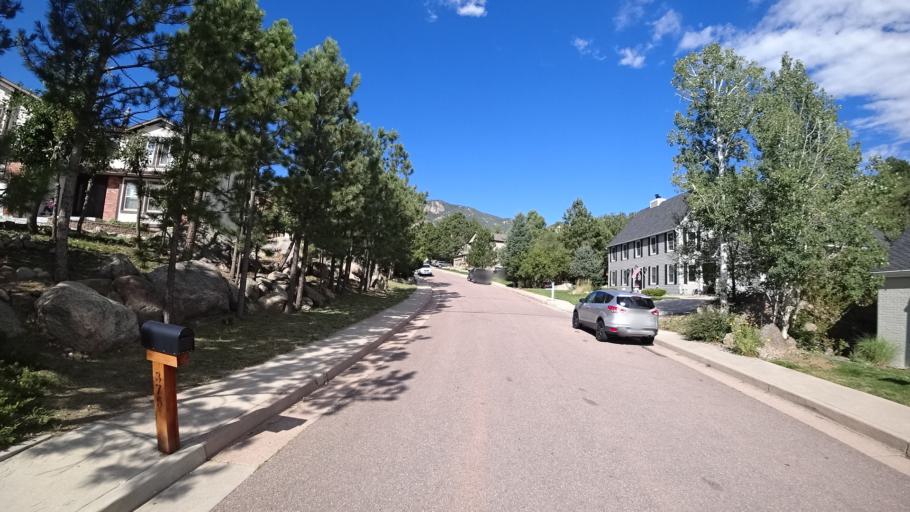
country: US
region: Colorado
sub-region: El Paso County
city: Stratmoor
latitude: 38.7674
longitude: -104.8250
